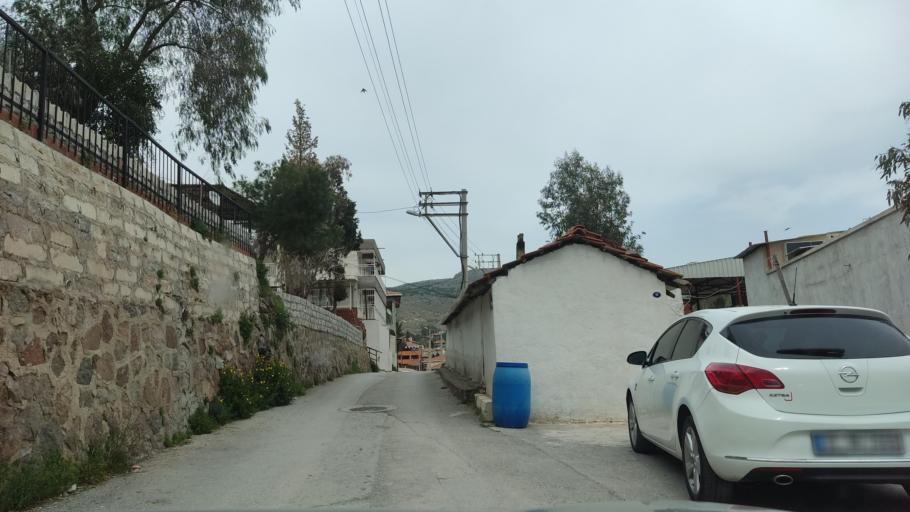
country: TR
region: Izmir
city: Karsiyaka
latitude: 38.4981
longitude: 27.0771
